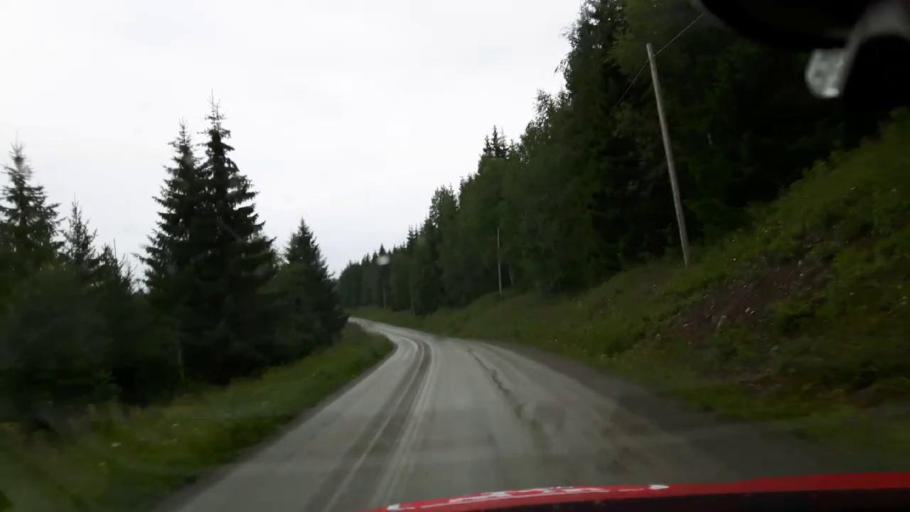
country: SE
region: Jaemtland
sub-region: OEstersunds Kommun
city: Brunflo
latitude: 62.8889
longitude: 14.8755
